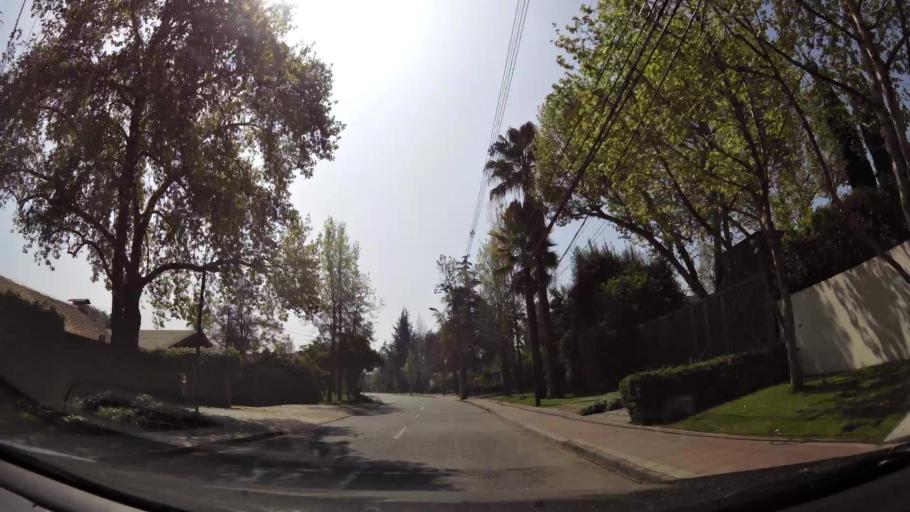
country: CL
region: Santiago Metropolitan
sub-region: Provincia de Santiago
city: Villa Presidente Frei, Nunoa, Santiago, Chile
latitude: -33.3957
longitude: -70.5857
